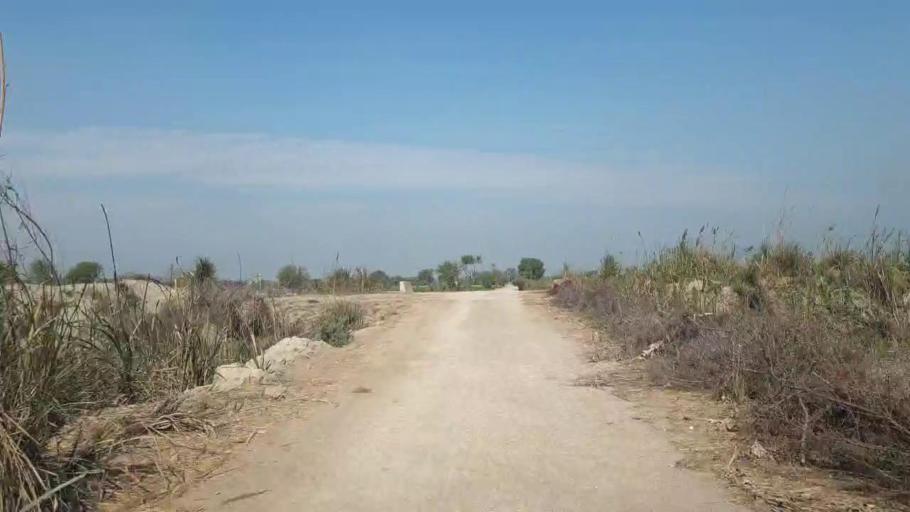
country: PK
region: Sindh
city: Shahdadpur
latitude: 25.9768
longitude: 68.5292
